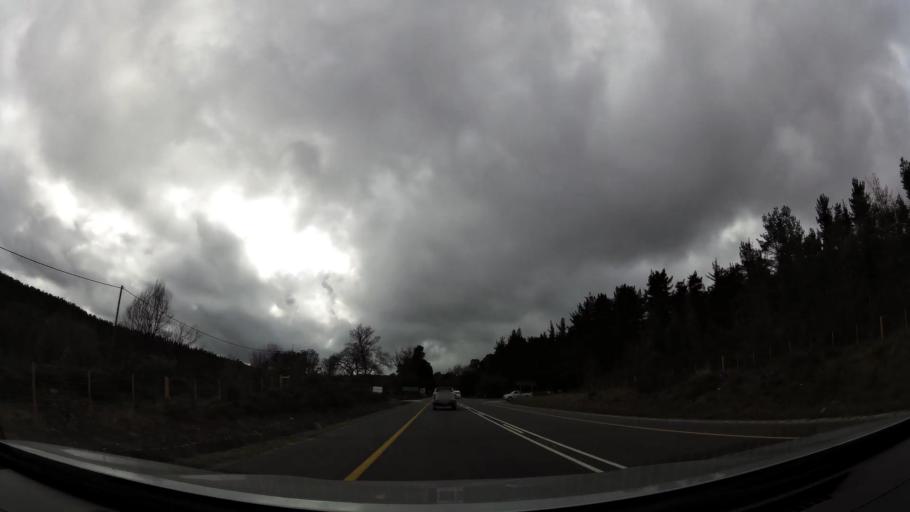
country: ZA
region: Western Cape
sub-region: Eden District Municipality
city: Knysna
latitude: -34.0301
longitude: 23.1591
